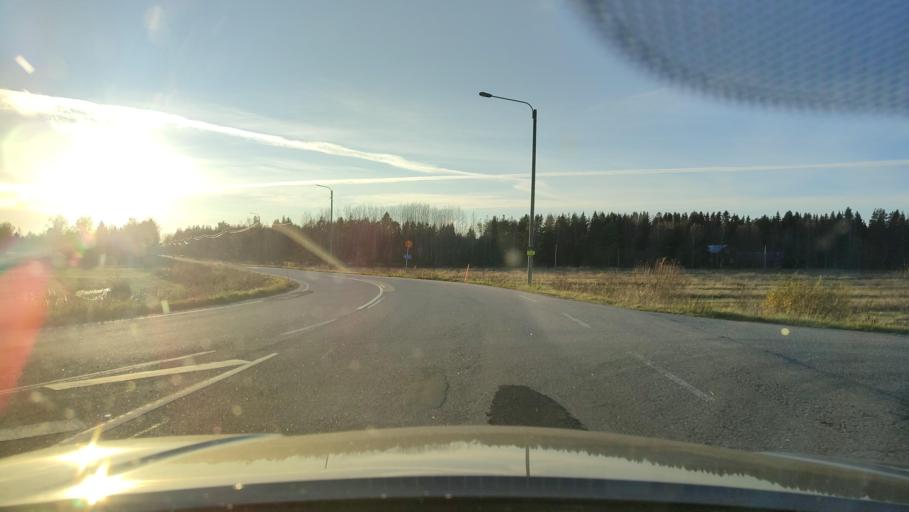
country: FI
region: Ostrobothnia
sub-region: Vaasa
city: Malax
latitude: 62.7086
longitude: 21.6074
